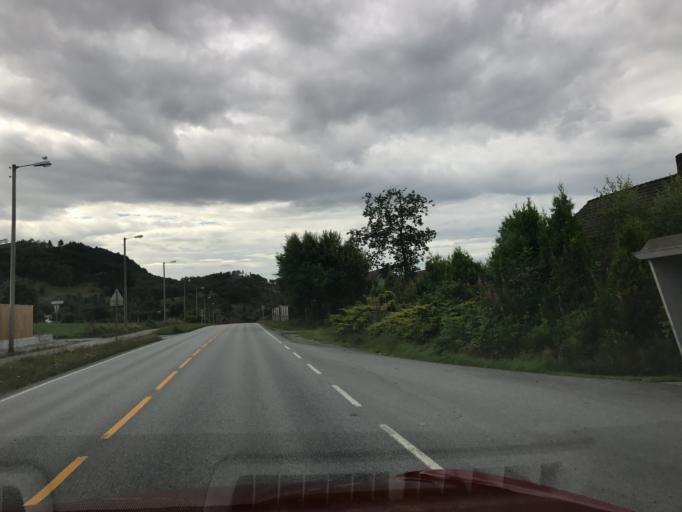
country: NO
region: Rogaland
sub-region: Strand
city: Tau
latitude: 59.0505
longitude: 5.9210
